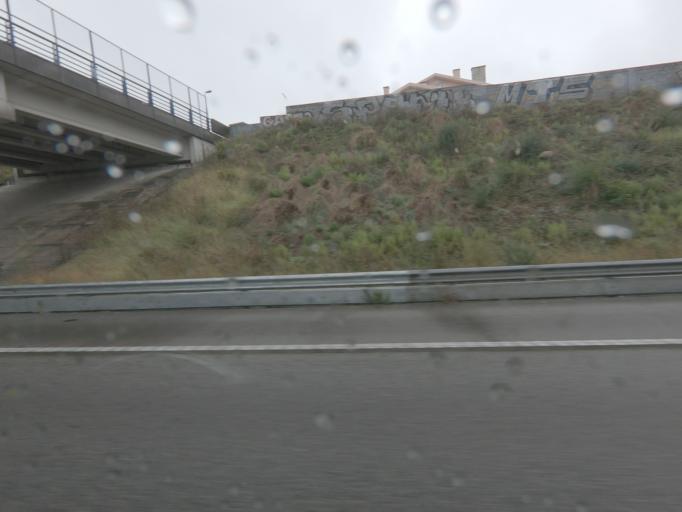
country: PT
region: Porto
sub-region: Matosinhos
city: Guifoes
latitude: 41.1966
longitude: -8.6636
